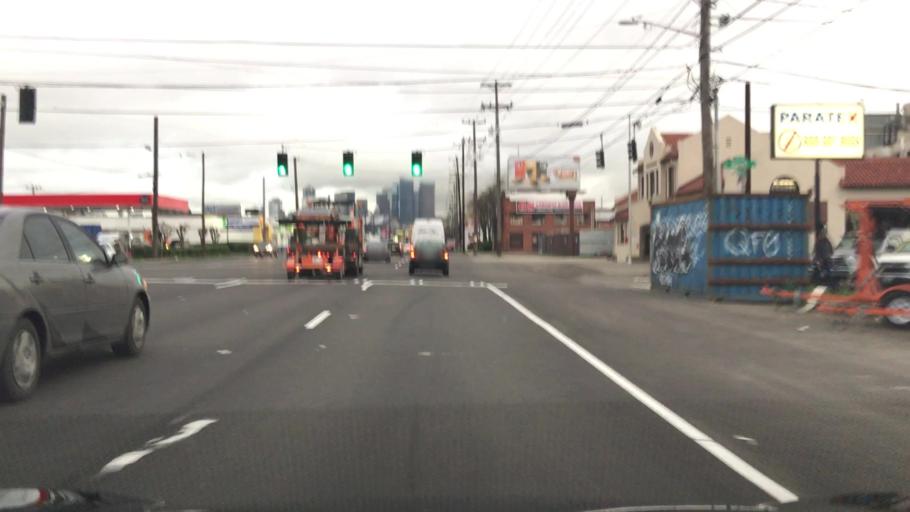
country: US
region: Washington
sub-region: King County
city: Seattle
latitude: 47.5741
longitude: -122.3289
